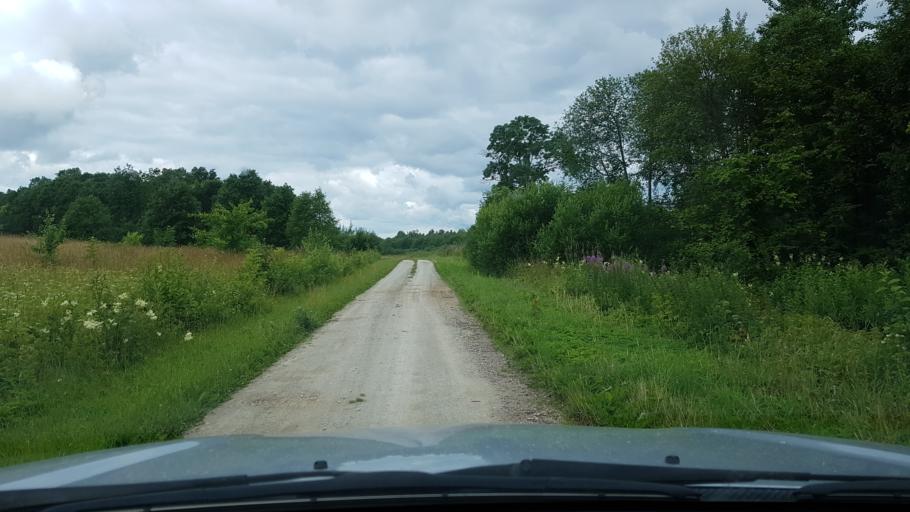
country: EE
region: Ida-Virumaa
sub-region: Narva-Joesuu linn
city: Narva-Joesuu
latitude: 59.4046
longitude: 27.9672
